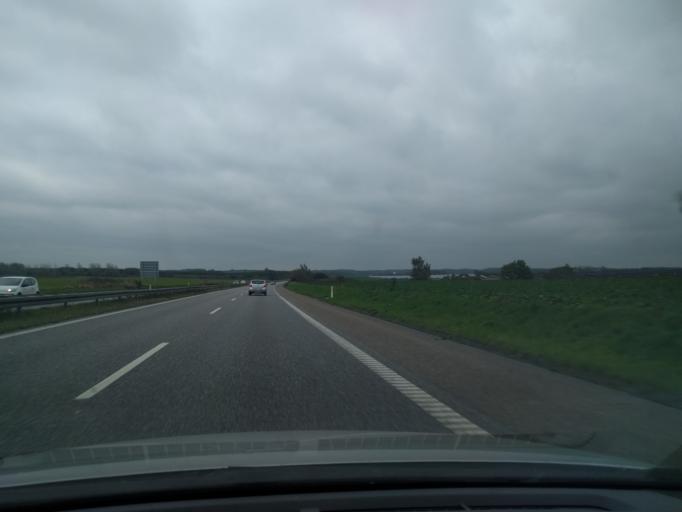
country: DK
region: Zealand
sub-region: Slagelse Kommune
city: Slagelse
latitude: 55.4280
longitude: 11.4342
